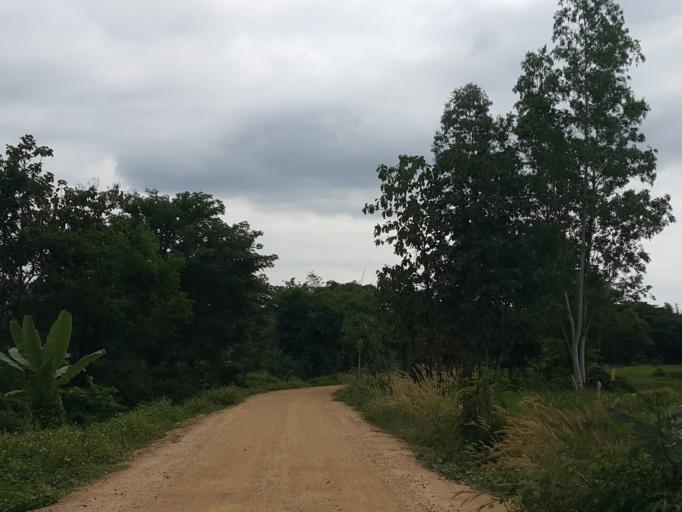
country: TH
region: Lampang
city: Hang Chat
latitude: 18.4731
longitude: 99.4160
